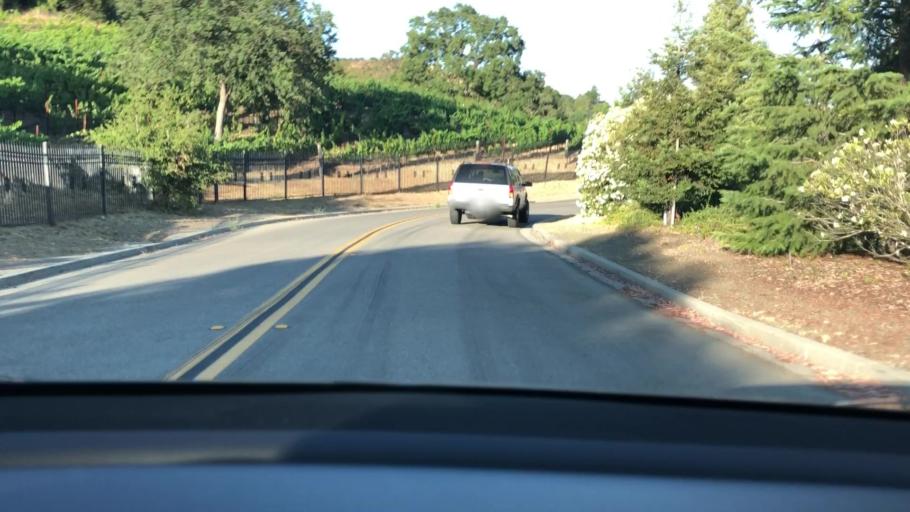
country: US
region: California
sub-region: Santa Clara County
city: Saratoga
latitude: 37.2752
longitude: -122.0676
